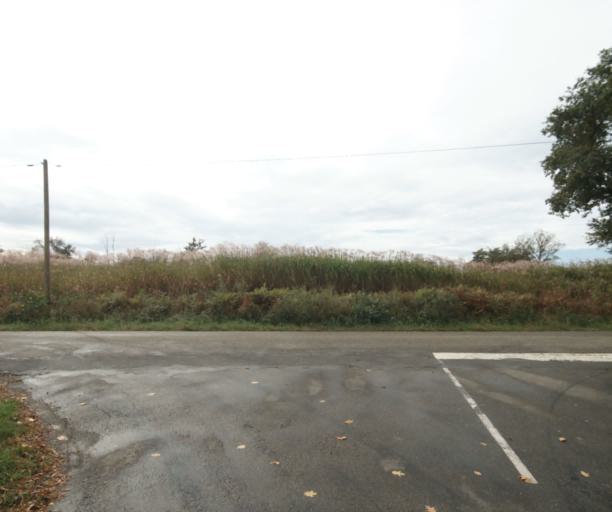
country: FR
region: Midi-Pyrenees
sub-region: Departement du Gers
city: Cazaubon
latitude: 43.9012
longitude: -0.1278
